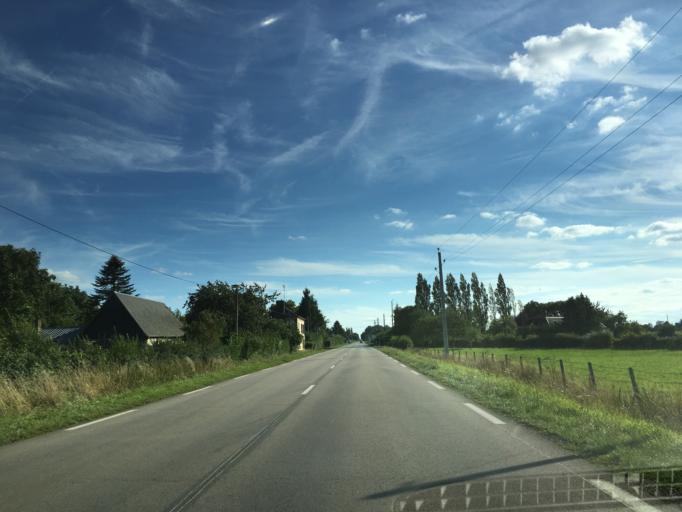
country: FR
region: Lower Normandy
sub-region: Departement du Calvados
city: Orbec
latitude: 48.9140
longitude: 0.4227
